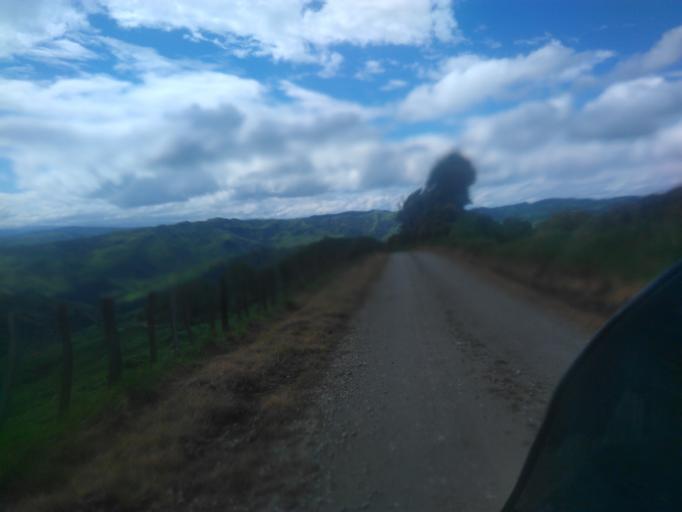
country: NZ
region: Hawke's Bay
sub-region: Wairoa District
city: Wairoa
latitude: -38.7690
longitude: 177.6398
